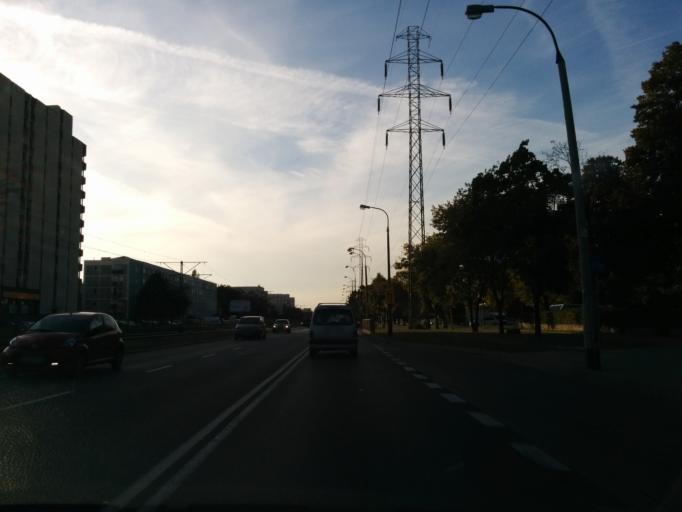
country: PL
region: Masovian Voivodeship
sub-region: Warszawa
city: Zoliborz
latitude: 52.2649
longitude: 20.9701
